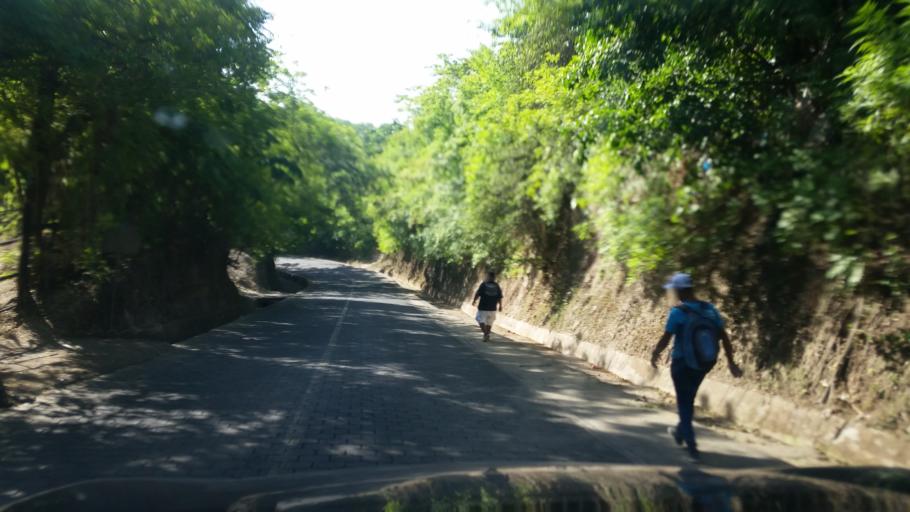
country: NI
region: Masaya
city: Catarina
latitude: 11.9547
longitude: -86.0443
